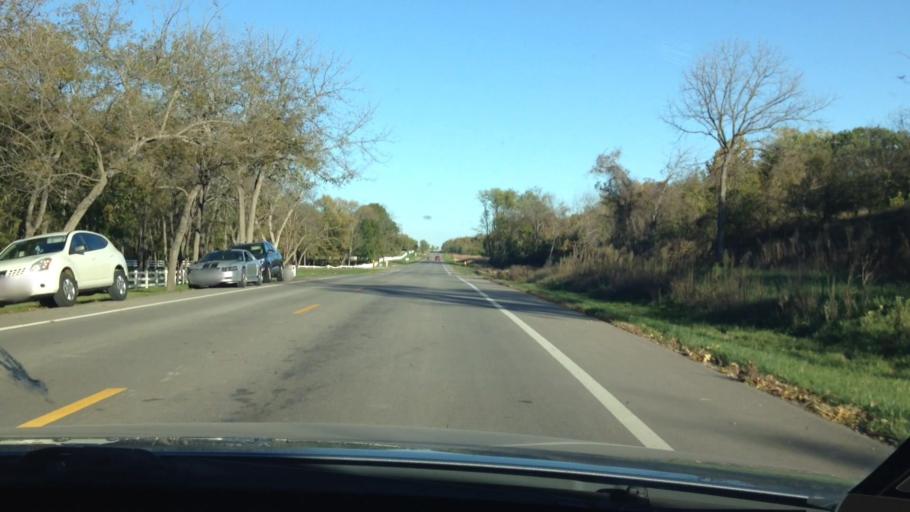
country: US
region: Kansas
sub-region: Johnson County
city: Edgerton
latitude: 38.7677
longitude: -94.9958
